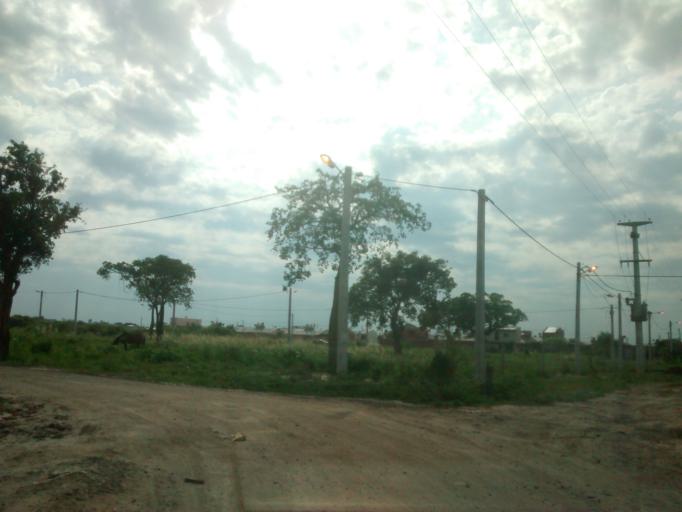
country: AR
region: Chaco
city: Fontana
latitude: -27.4026
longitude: -58.9837
